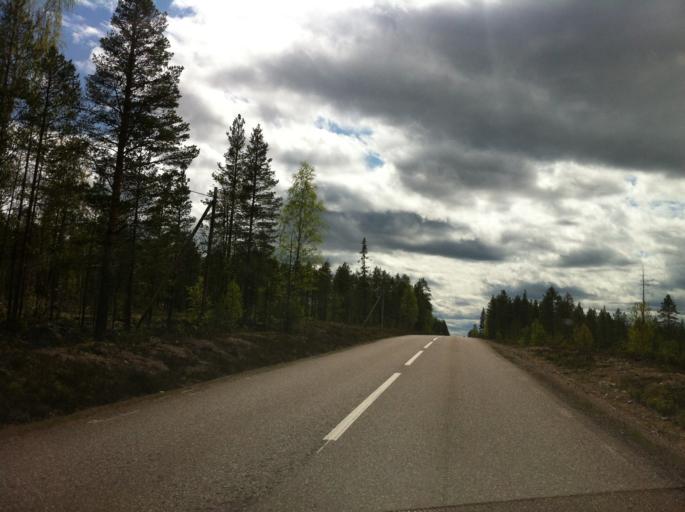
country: NO
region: Hedmark
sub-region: Trysil
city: Innbygda
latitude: 61.6789
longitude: 13.1256
